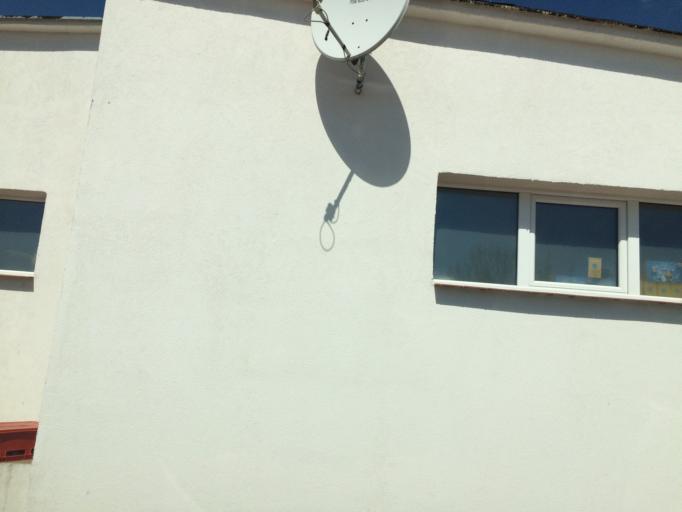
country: PL
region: Warmian-Masurian Voivodeship
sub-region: Powiat nowomiejski
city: Biskupiec
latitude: 53.4450
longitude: 19.3515
